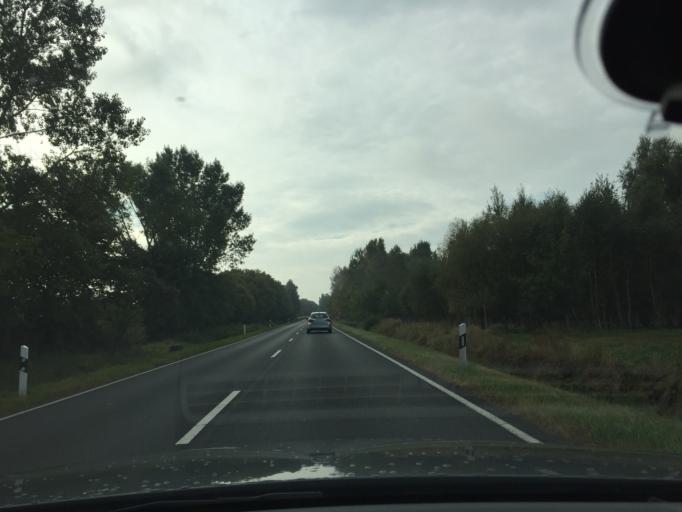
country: DE
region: Mecklenburg-Vorpommern
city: Ostseebad Dierhagen
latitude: 54.2344
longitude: 12.3638
